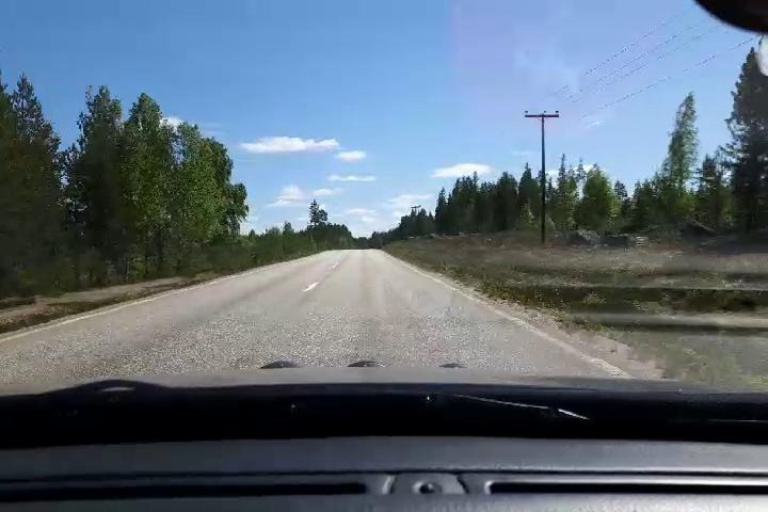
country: SE
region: Vaesternorrland
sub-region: Ange Kommun
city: Ange
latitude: 62.0954
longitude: 15.0826
